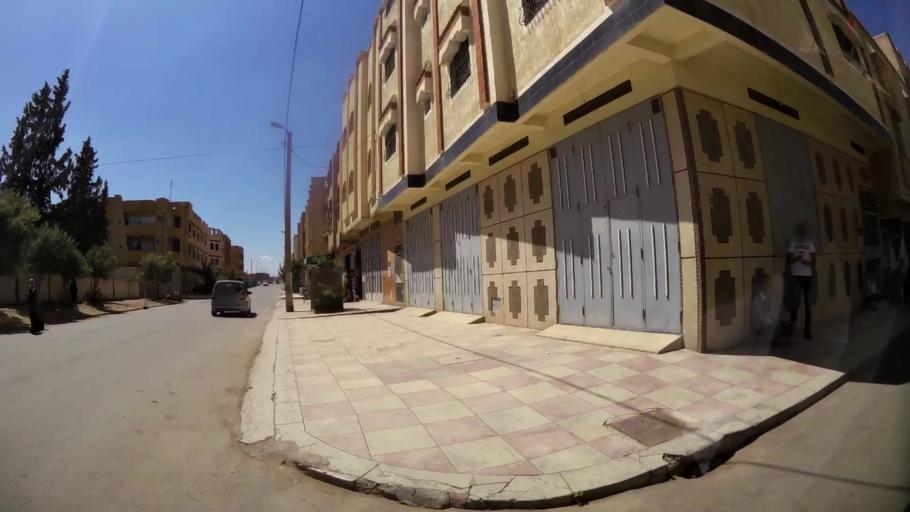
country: MA
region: Oriental
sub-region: Oujda-Angad
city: Oujda
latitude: 34.6869
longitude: -1.9384
